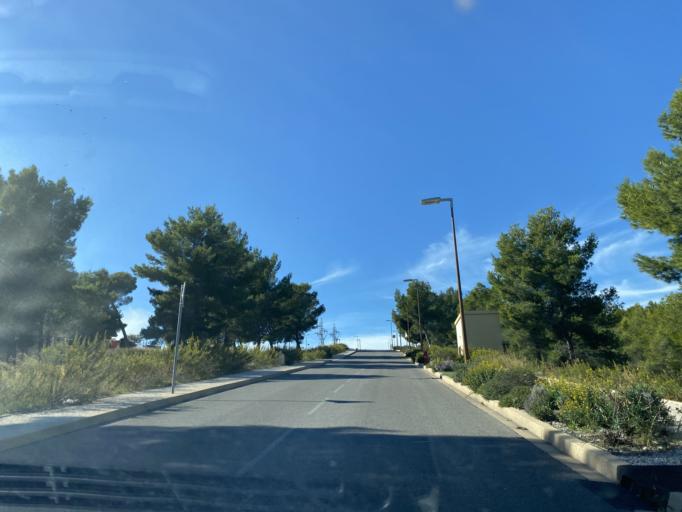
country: FR
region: Provence-Alpes-Cote d'Azur
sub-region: Departement des Bouches-du-Rhone
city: Ceyreste
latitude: 43.2117
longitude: 5.5966
